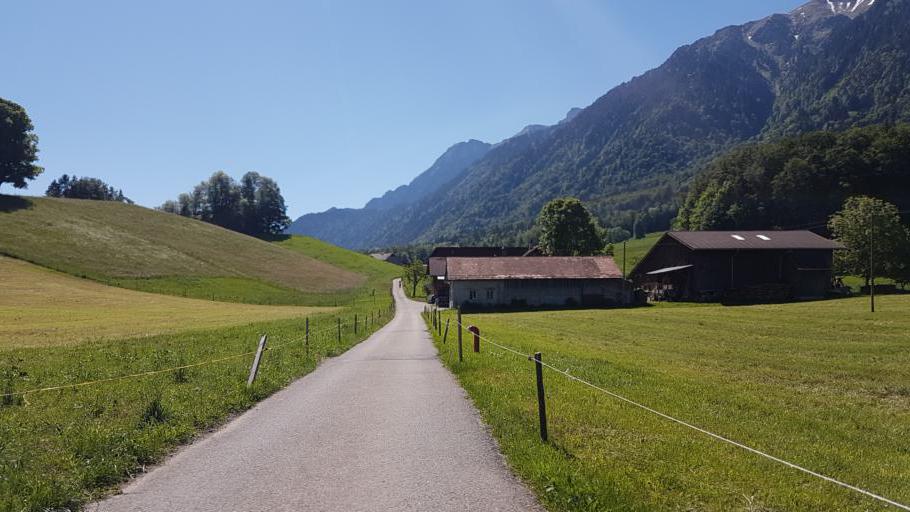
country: CH
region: Bern
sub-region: Thun District
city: Blumenstein
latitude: 46.7302
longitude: 7.5203
